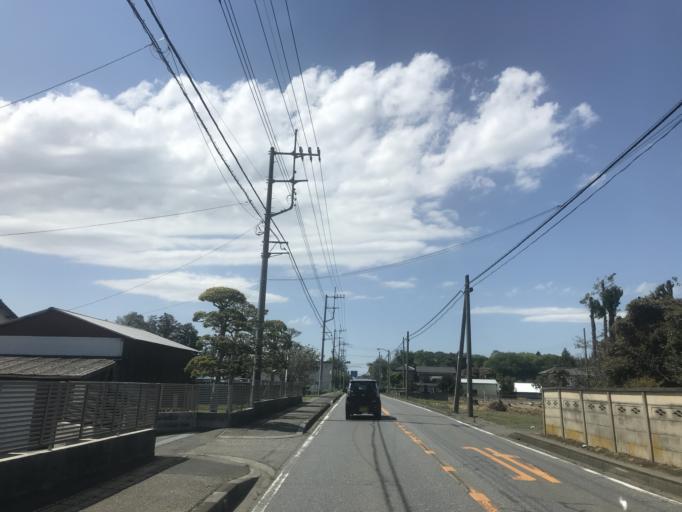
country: JP
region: Chiba
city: Noda
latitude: 35.9451
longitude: 139.9135
